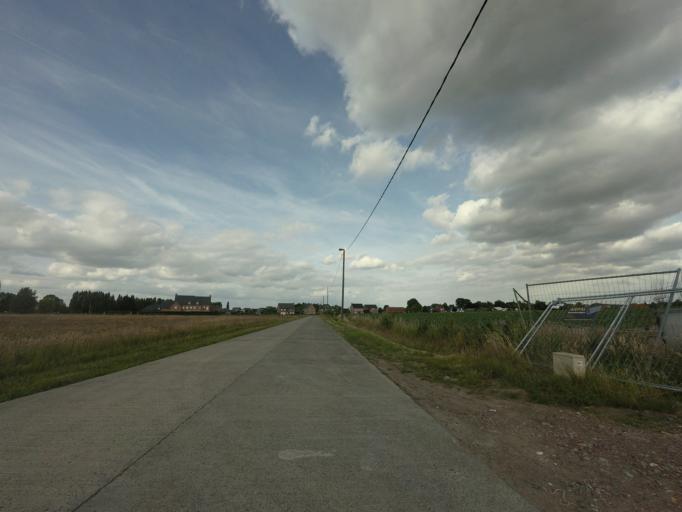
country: BE
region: Flanders
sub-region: Provincie Antwerpen
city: Duffel
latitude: 51.0982
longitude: 4.4808
